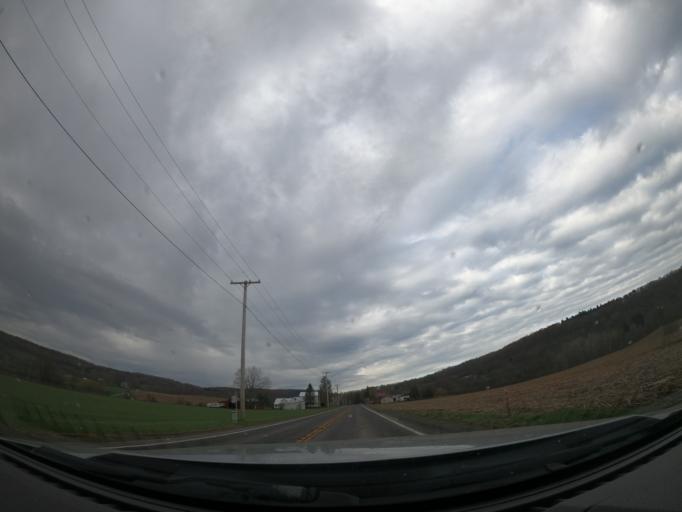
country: US
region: New York
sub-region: Madison County
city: Cazenovia
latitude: 42.8074
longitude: -75.8366
